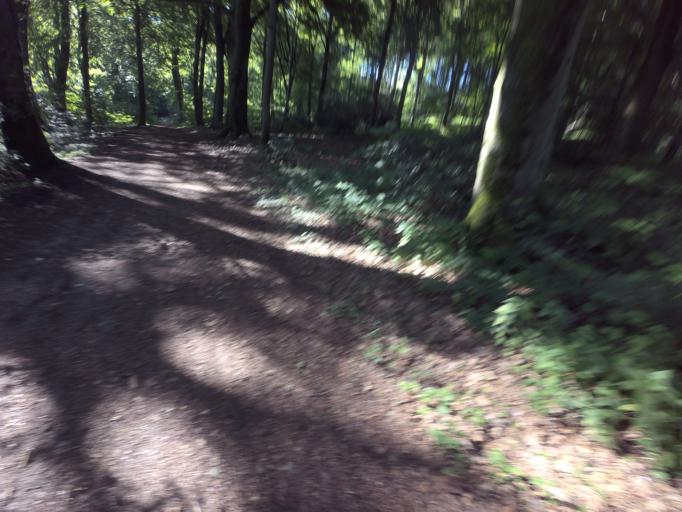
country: NL
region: Limburg
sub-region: Gemeente Vaals
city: Vaals
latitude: 50.7589
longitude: 6.0224
